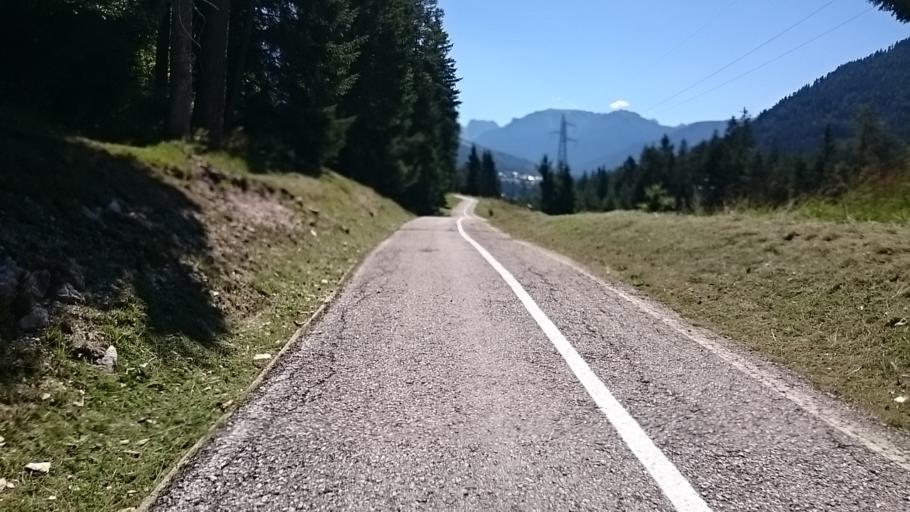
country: IT
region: Veneto
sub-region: Provincia di Belluno
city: San Vito
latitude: 46.4892
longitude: 12.1849
